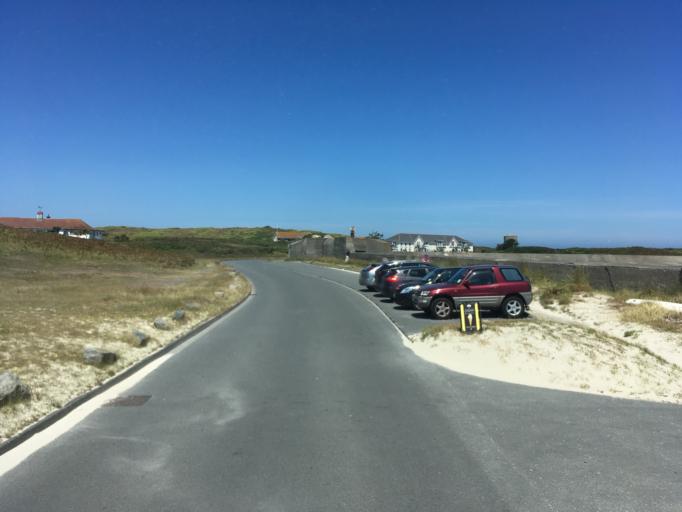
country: GG
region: St Peter Port
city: Saint Peter Port
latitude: 49.5037
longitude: -2.5335
